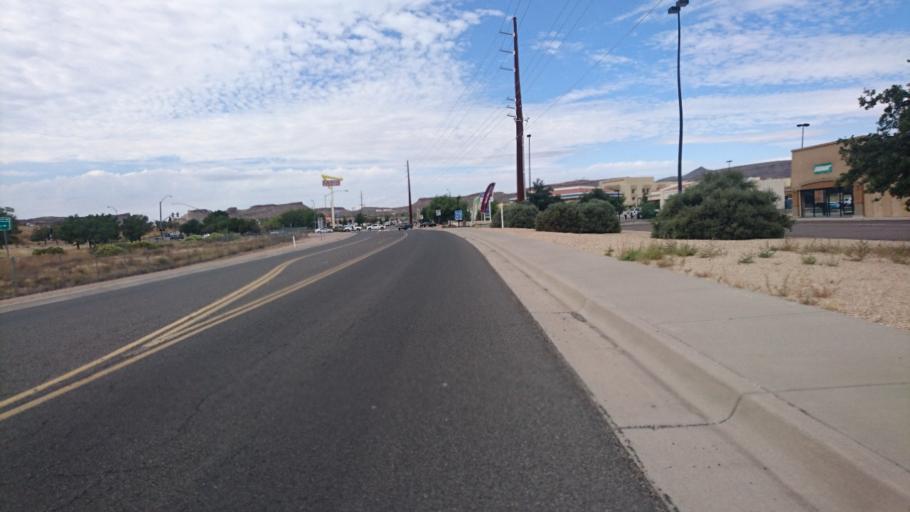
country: US
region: Arizona
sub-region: Mohave County
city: Kingman
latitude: 35.2188
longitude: -114.0339
